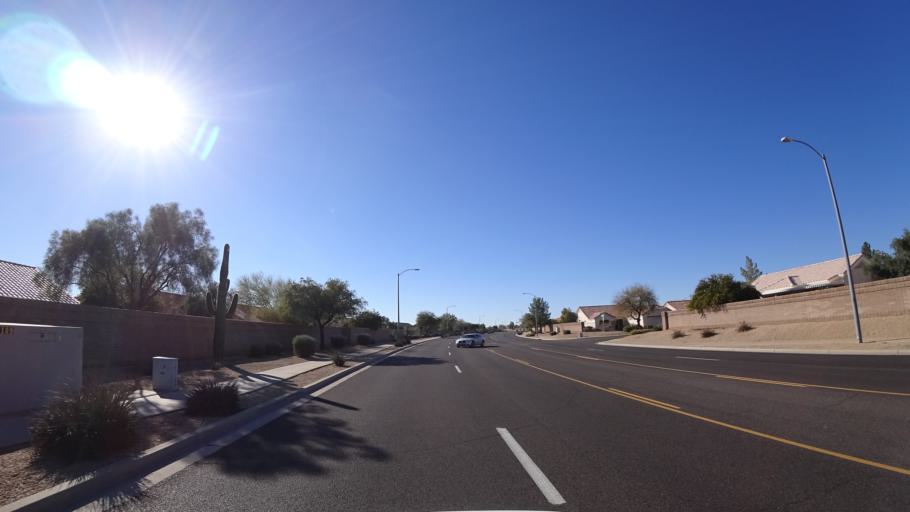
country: US
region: Arizona
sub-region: Maricopa County
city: Sun City West
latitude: 33.6872
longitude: -112.3652
